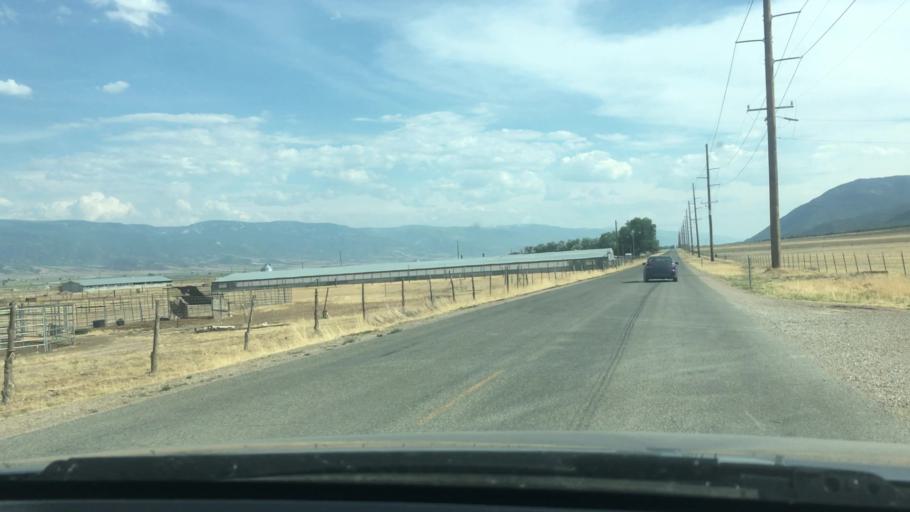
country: US
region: Utah
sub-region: Sanpete County
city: Moroni
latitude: 39.5302
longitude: -111.6398
